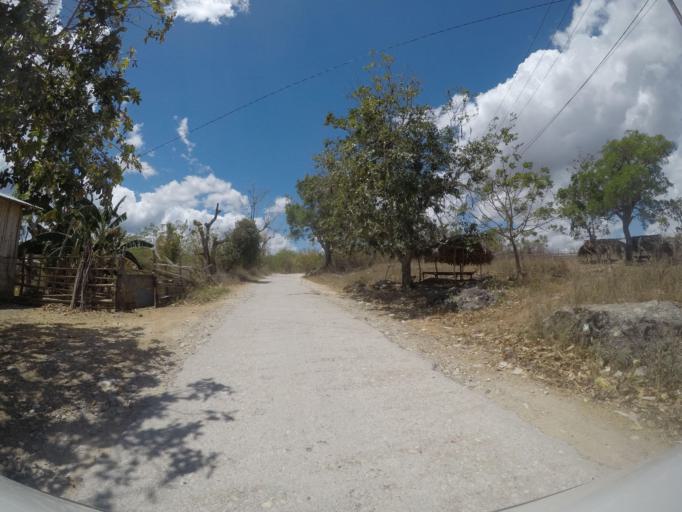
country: TL
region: Baucau
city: Baucau
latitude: -8.4836
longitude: 126.6264
